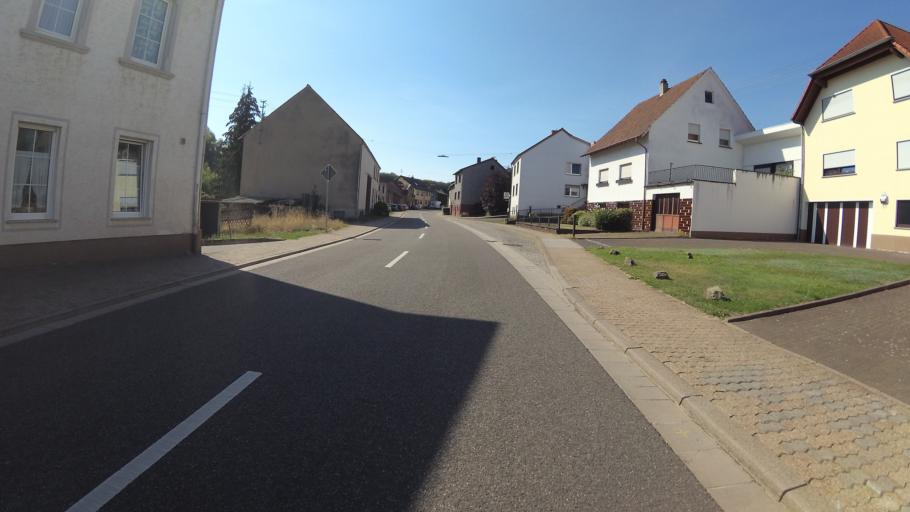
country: DE
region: Saarland
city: Eppelborn
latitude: 49.3746
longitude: 6.9744
